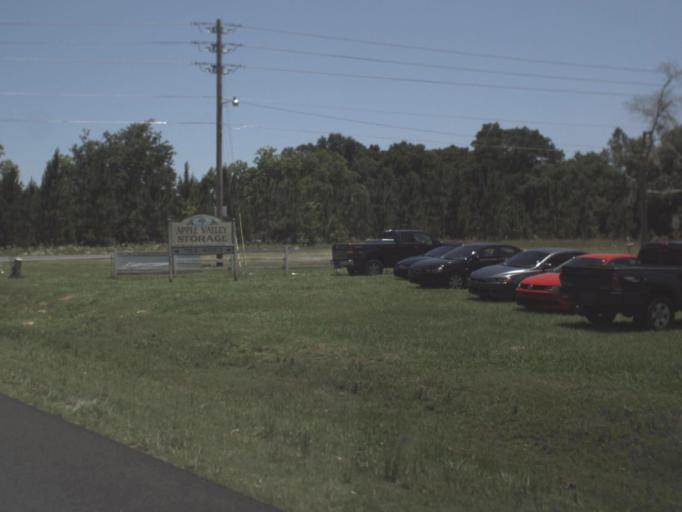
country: US
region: Florida
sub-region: Suwannee County
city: Wellborn
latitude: 30.1925
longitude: -82.7345
